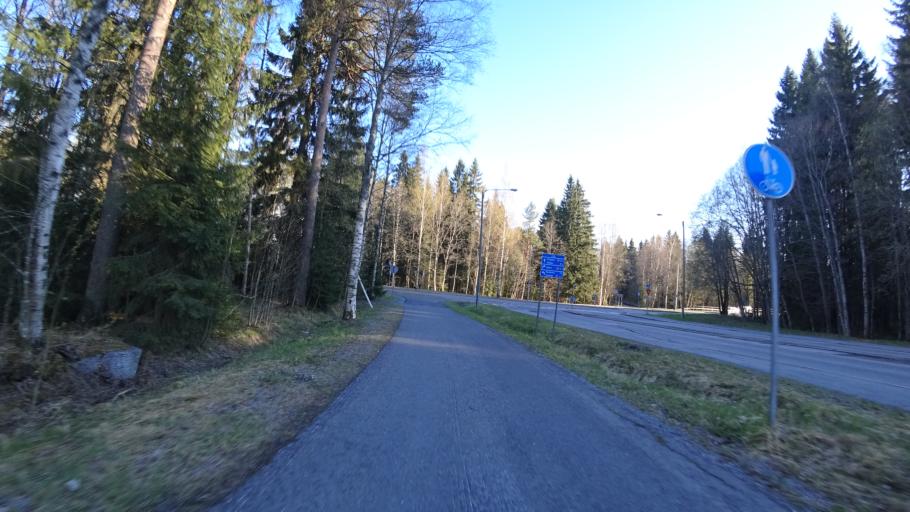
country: FI
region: Pirkanmaa
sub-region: Tampere
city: Yloejaervi
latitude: 61.5045
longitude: 23.5922
